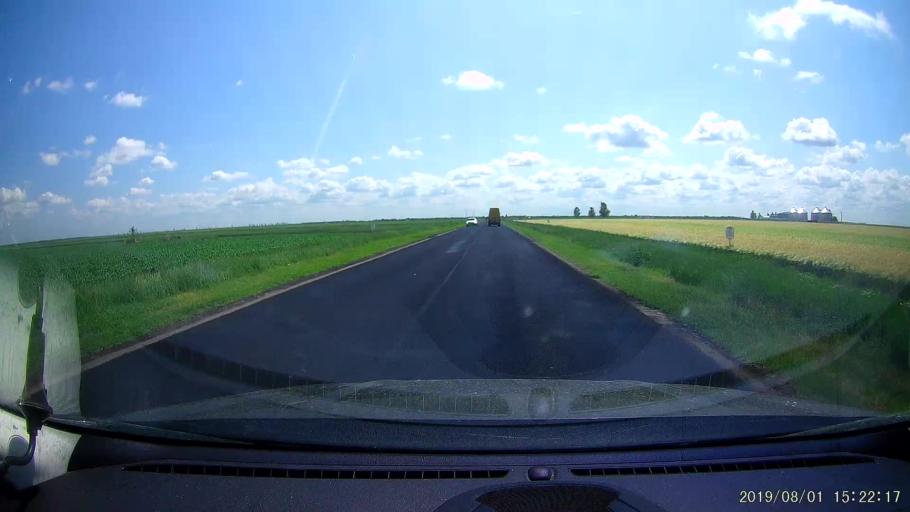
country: RO
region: Braila
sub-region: Comuna Viziru
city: Lanurile
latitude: 45.0557
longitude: 27.7788
